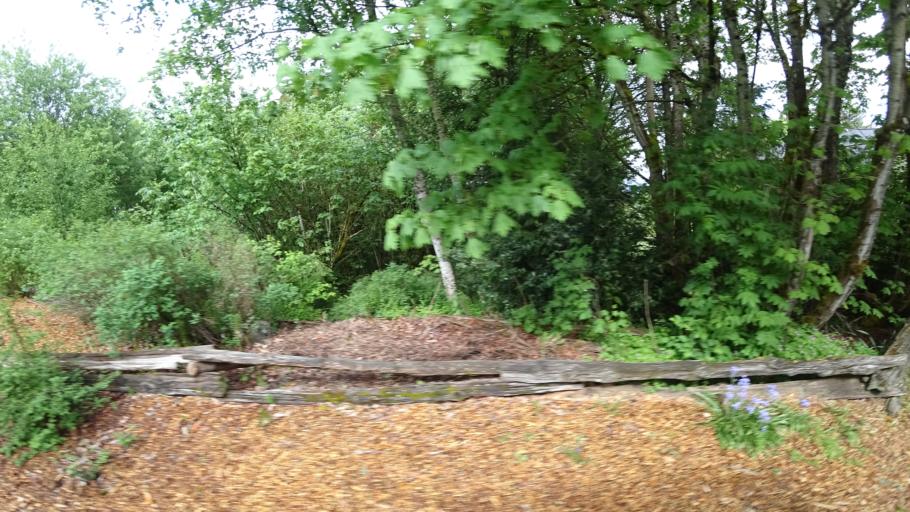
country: US
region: Oregon
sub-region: Washington County
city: West Haven
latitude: 45.5355
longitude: -122.7543
